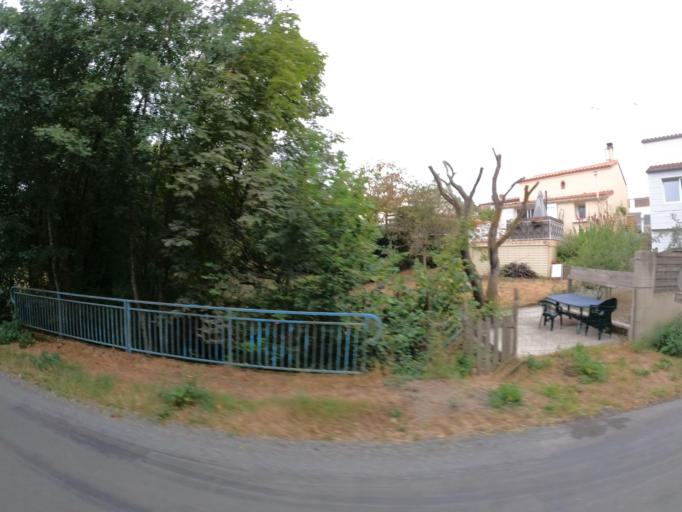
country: FR
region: Pays de la Loire
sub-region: Departement de la Vendee
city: Montaigu
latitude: 46.9736
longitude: -1.2875
